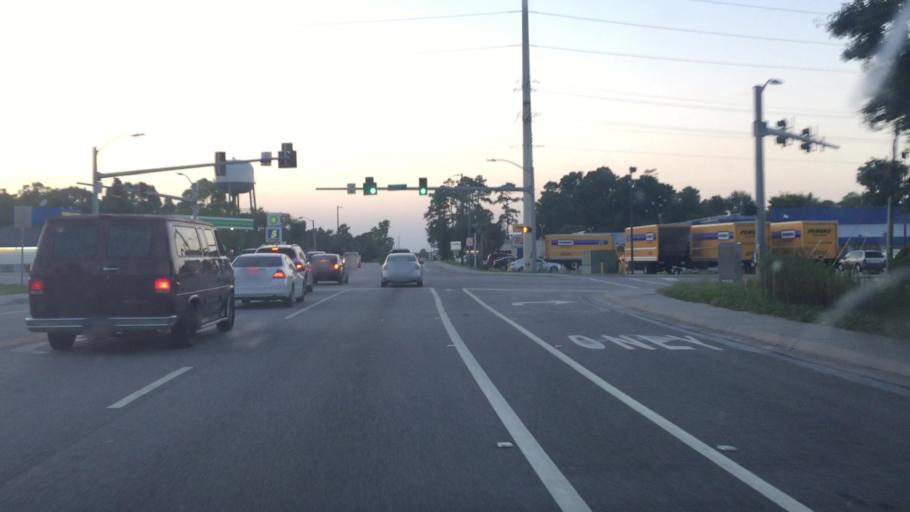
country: US
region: South Carolina
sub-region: Horry County
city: Myrtle Beach
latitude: 33.6907
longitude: -78.8961
